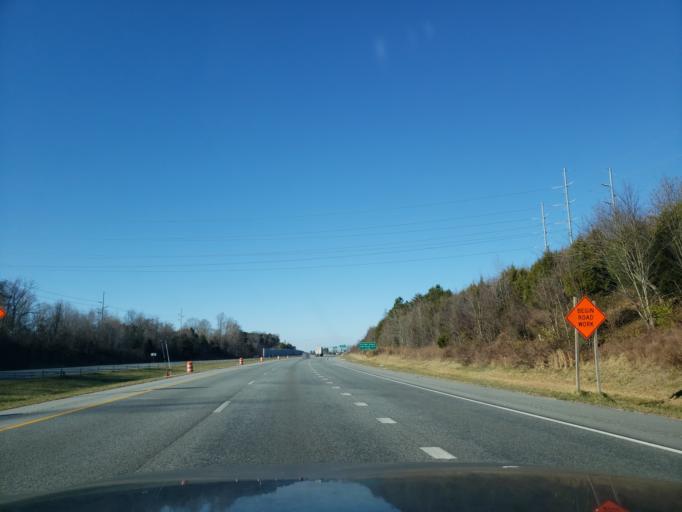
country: US
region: North Carolina
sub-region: Guilford County
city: High Point
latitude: 35.9935
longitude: -79.9853
